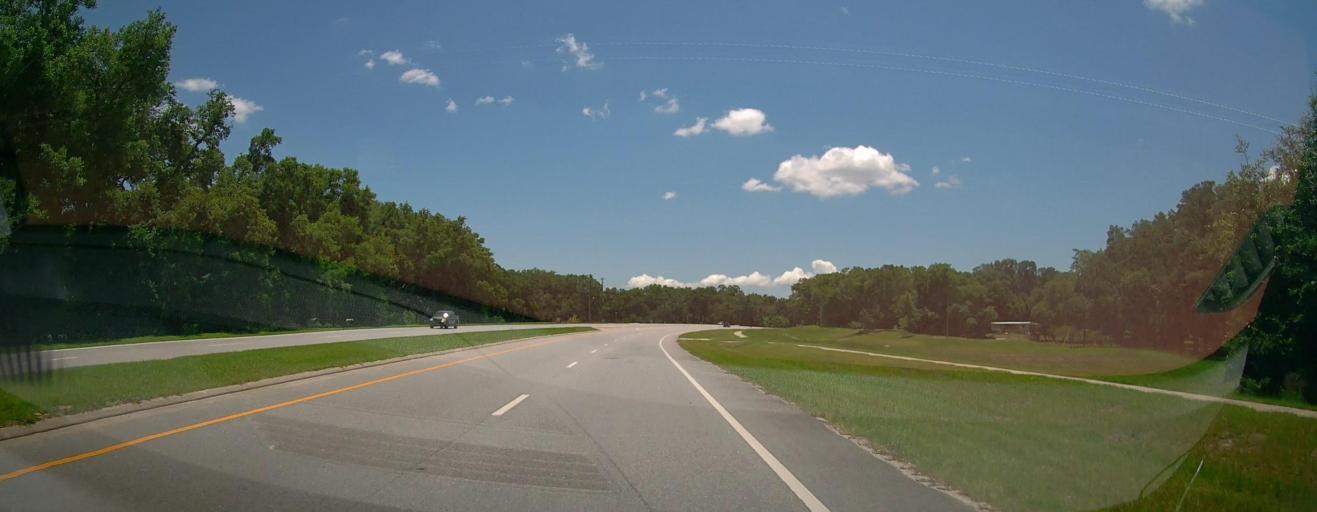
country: US
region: Florida
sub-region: Marion County
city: Belleview
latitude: 29.0372
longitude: -82.0177
